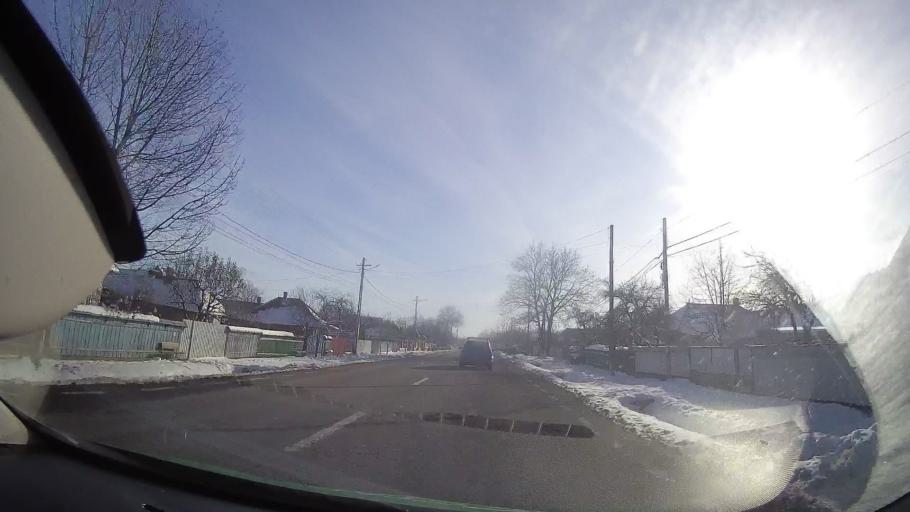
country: RO
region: Neamt
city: Bodesti
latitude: 47.0403
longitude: 26.4077
